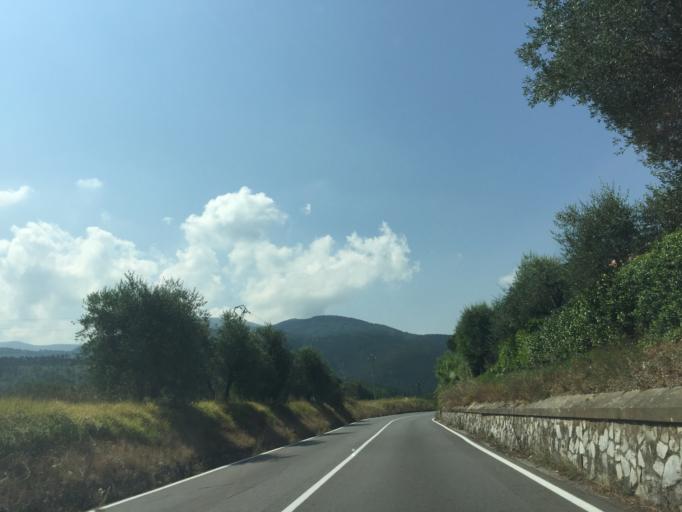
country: IT
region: Tuscany
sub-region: Provincia di Lucca
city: Lucca
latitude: 43.8007
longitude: 10.4846
